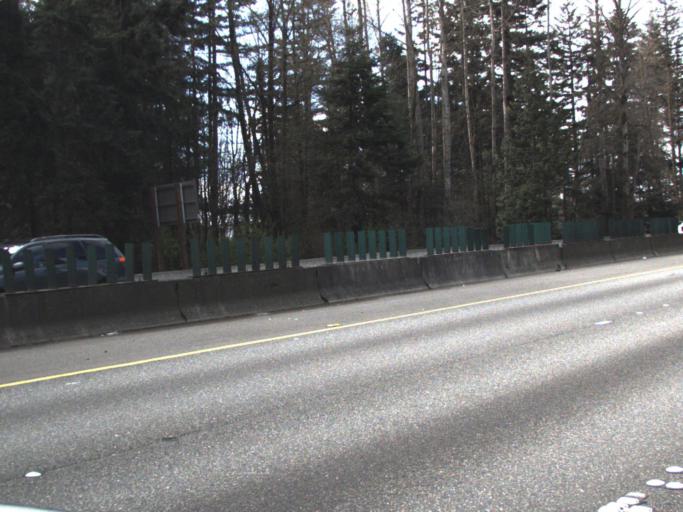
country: US
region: Washington
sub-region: King County
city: Lakeland South
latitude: 47.3004
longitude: -122.2806
